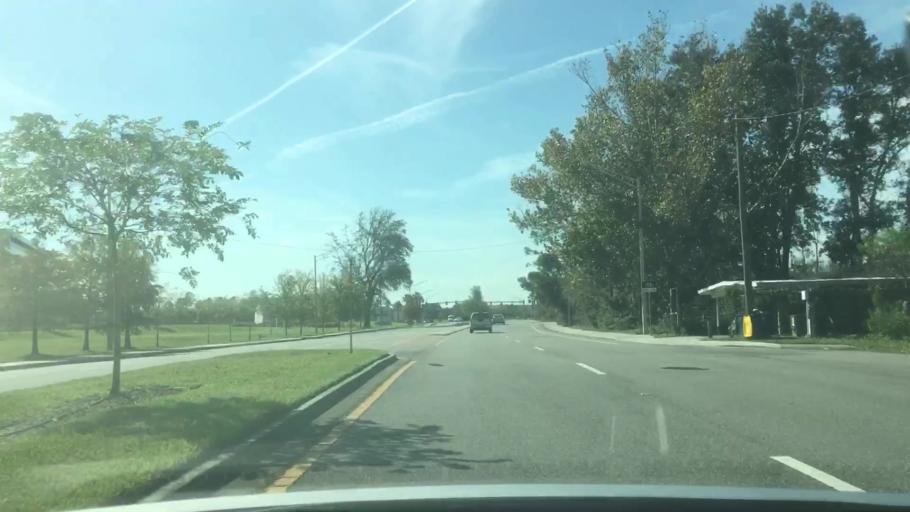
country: US
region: Florida
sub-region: Nassau County
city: Yulee
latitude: 30.4868
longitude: -81.6340
